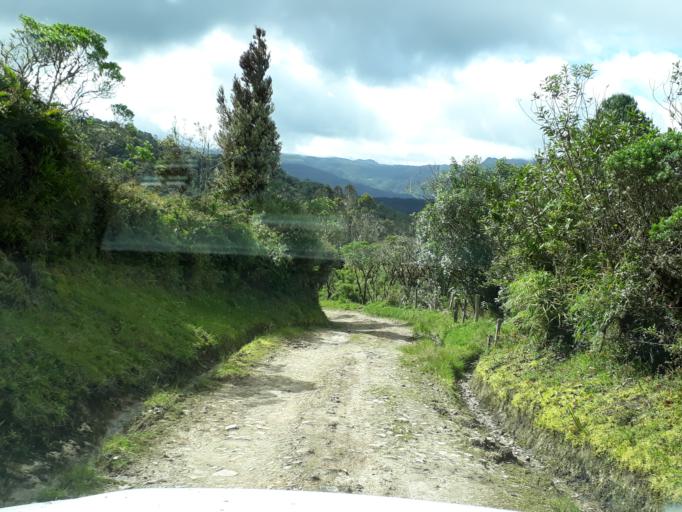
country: CO
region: Cundinamarca
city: Junin
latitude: 4.7808
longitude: -73.7747
